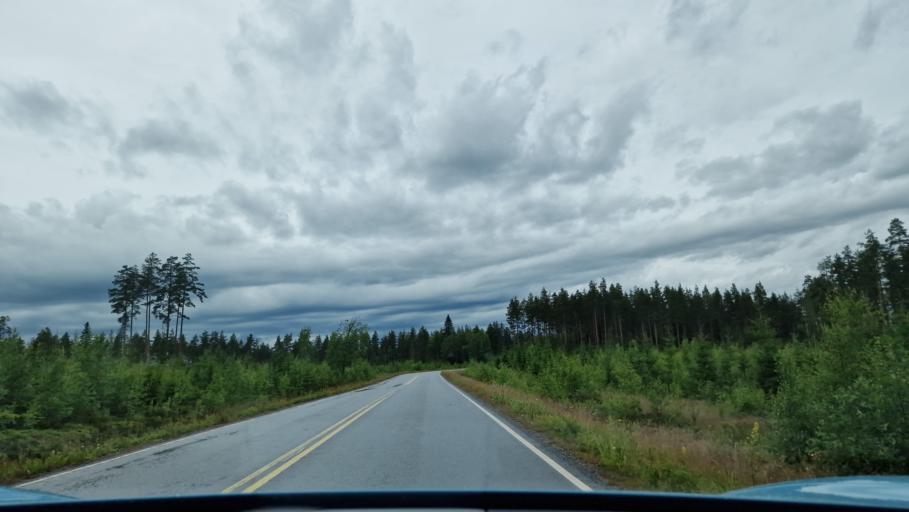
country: FI
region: Central Finland
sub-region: Saarijaervi-Viitasaari
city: Pylkoenmaeki
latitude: 62.6707
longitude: 24.5149
